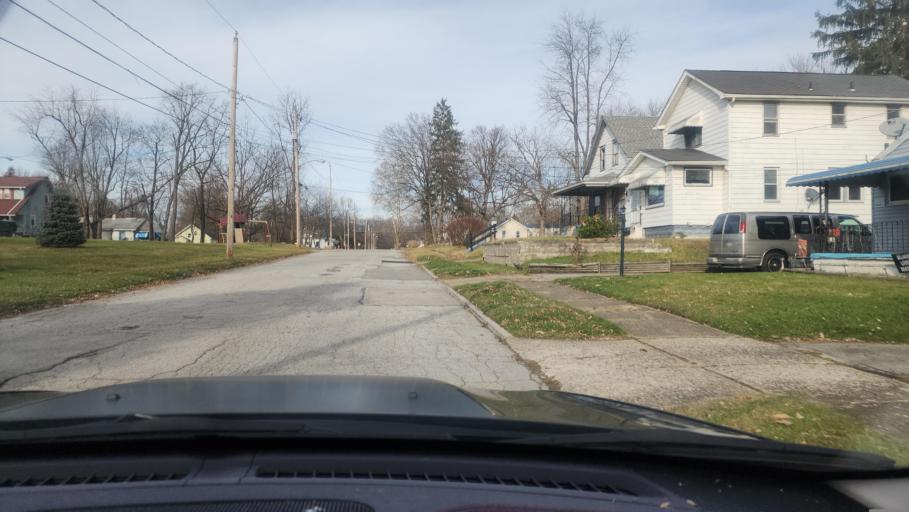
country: US
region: Ohio
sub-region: Mahoning County
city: Campbell
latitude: 41.1036
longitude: -80.6173
